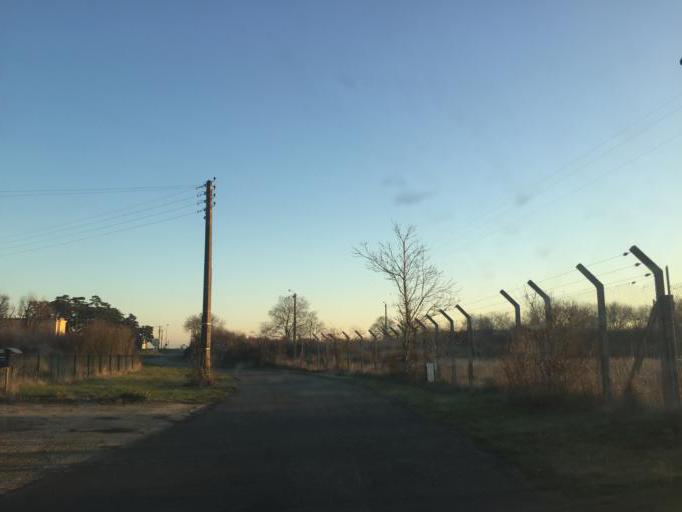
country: FR
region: Rhone-Alpes
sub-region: Departement de l'Ain
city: Beligneux
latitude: 45.8547
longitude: 5.1415
